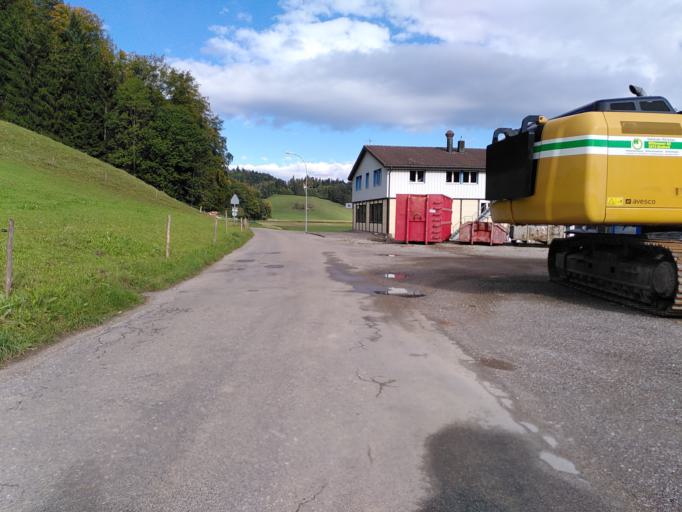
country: CH
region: Bern
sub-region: Oberaargau
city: Seeberg
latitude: 47.1448
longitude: 7.6949
